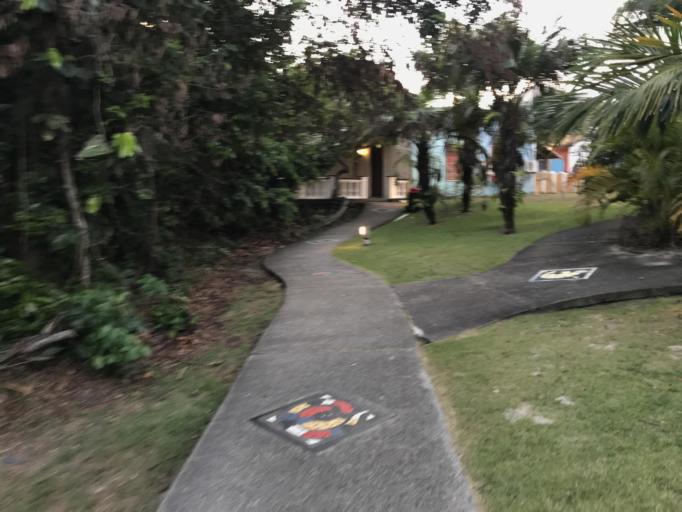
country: BR
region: Bahia
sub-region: Mata De Sao Joao
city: Mata de Sao Joao
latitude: -12.4407
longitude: -37.9218
